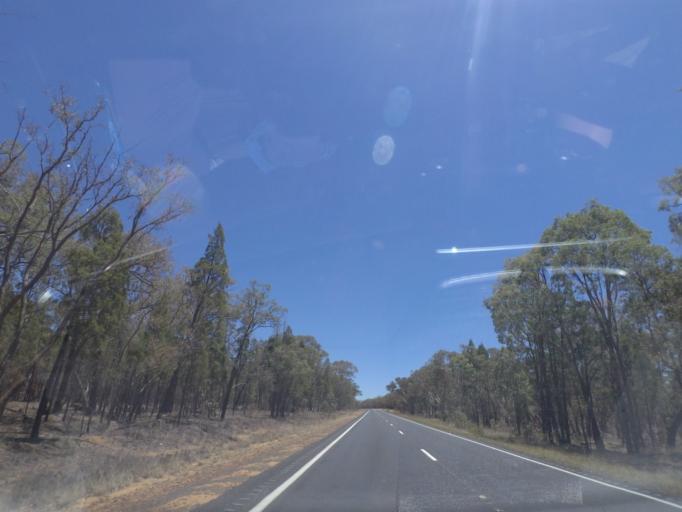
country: AU
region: New South Wales
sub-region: Warrumbungle Shire
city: Coonabarabran
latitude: -31.2021
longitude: 149.3405
